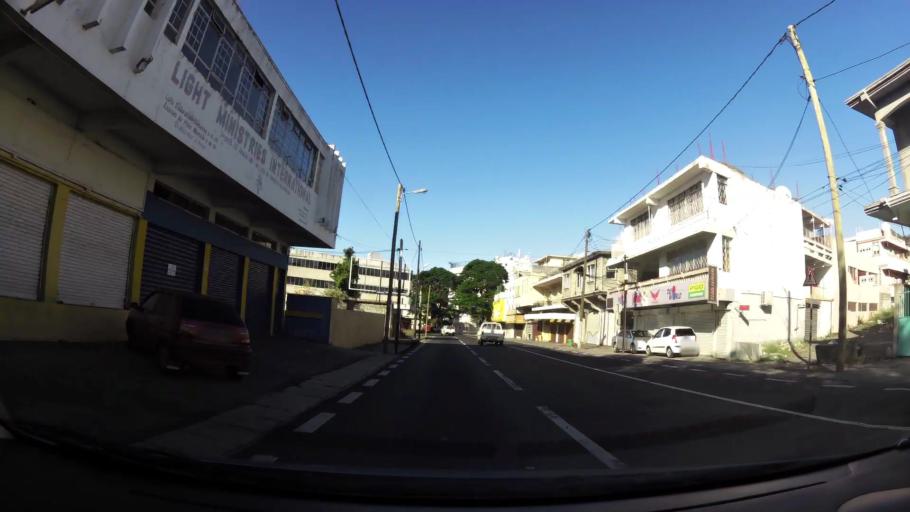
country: MU
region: Port Louis
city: Port Louis
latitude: -20.1654
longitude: 57.4943
